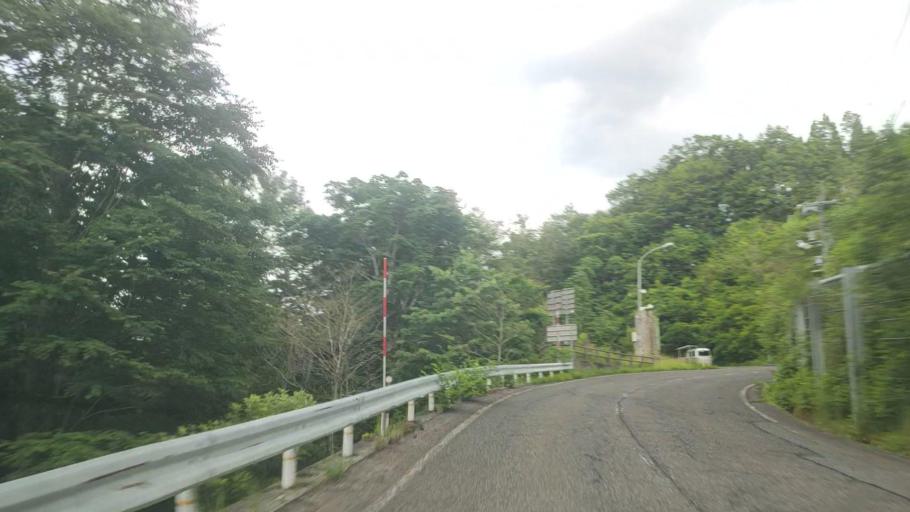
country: JP
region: Tottori
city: Kurayoshi
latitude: 35.3133
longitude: 134.0033
